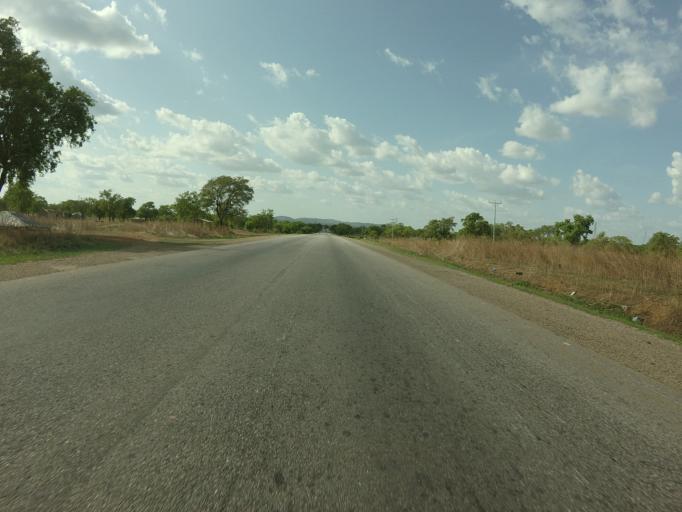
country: GH
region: Upper East
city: Bolgatanga
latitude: 10.5729
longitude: -0.8329
